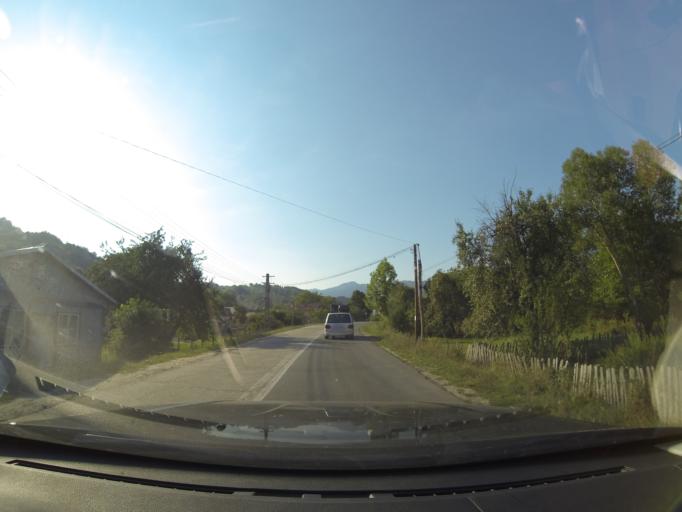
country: RO
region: Arges
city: Poenari
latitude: 45.3197
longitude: 24.6408
